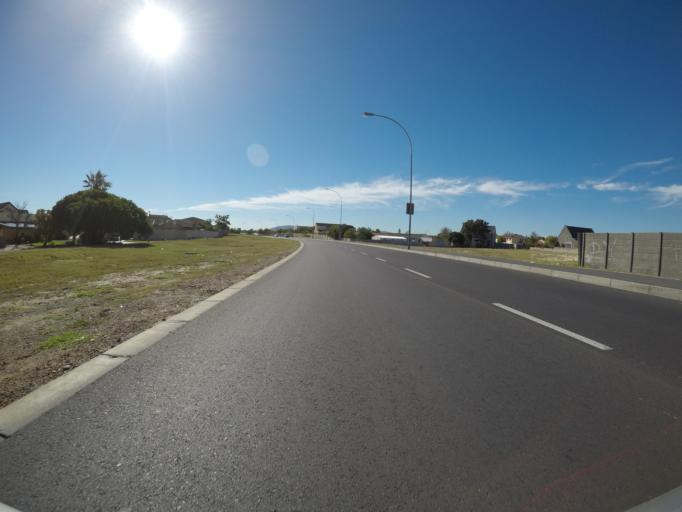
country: ZA
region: Western Cape
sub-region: City of Cape Town
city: Kraaifontein
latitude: -33.9444
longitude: 18.6807
